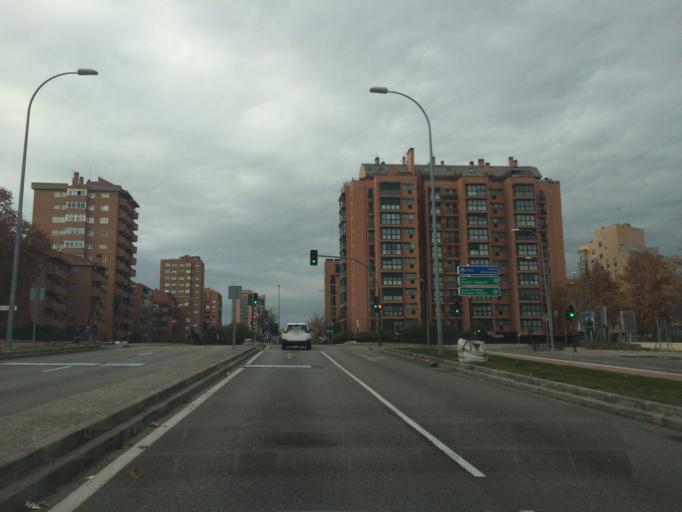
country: ES
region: Madrid
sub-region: Provincia de Madrid
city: Tetuan de las Victorias
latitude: 40.4709
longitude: -3.7190
